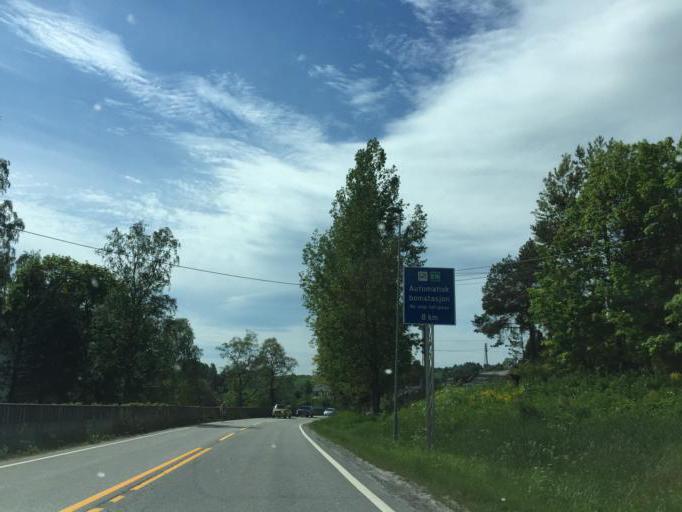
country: NO
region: Akershus
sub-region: Nes
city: Arnes
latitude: 60.1567
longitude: 11.4207
